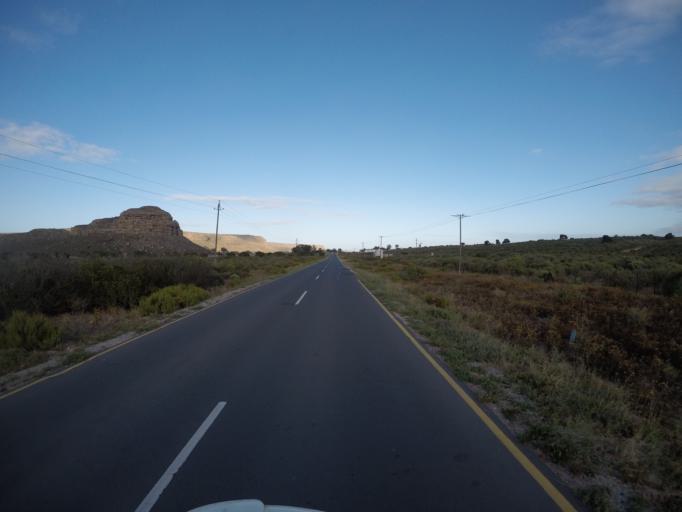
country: ZA
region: Western Cape
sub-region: West Coast District Municipality
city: Clanwilliam
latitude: -32.3129
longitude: 18.3617
